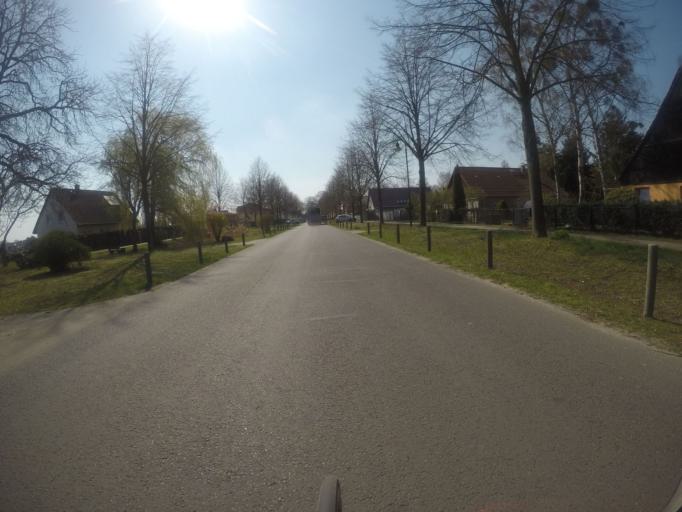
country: DE
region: Brandenburg
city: Falkensee
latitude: 52.6180
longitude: 13.1264
